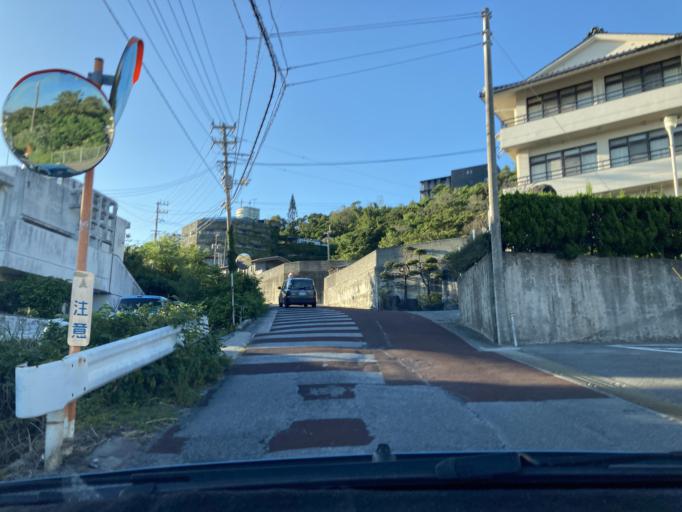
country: JP
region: Okinawa
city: Naha-shi
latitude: 26.2102
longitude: 127.7334
